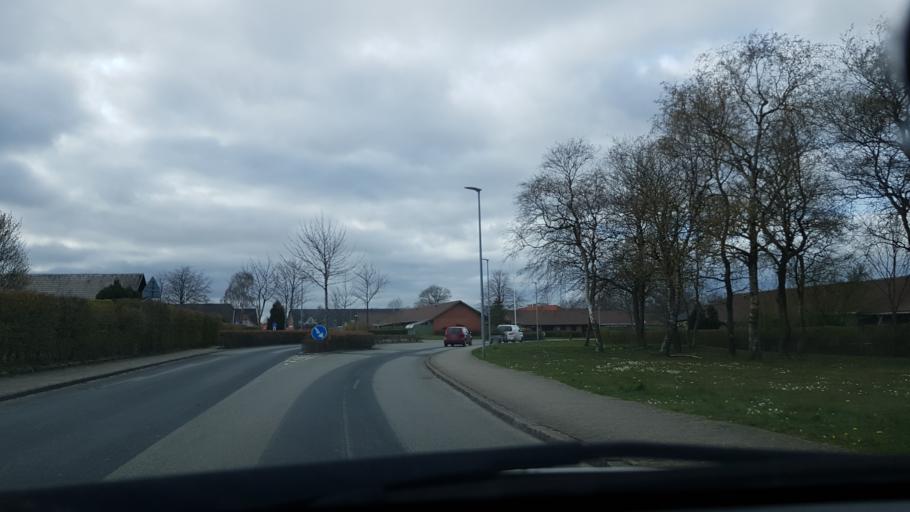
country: DK
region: South Denmark
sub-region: Vejen Kommune
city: Vejen
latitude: 55.4709
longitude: 9.1450
